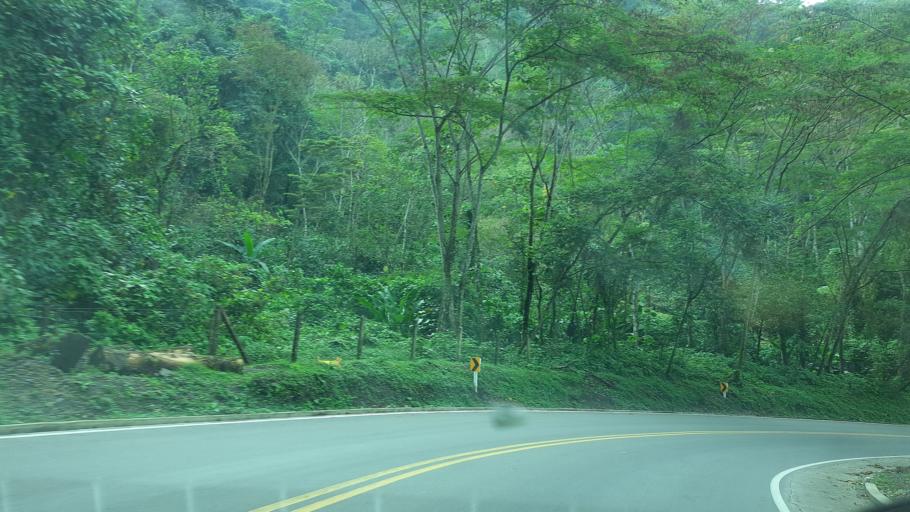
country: CO
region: Boyaca
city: Santa Maria
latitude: 4.8683
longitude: -73.2529
